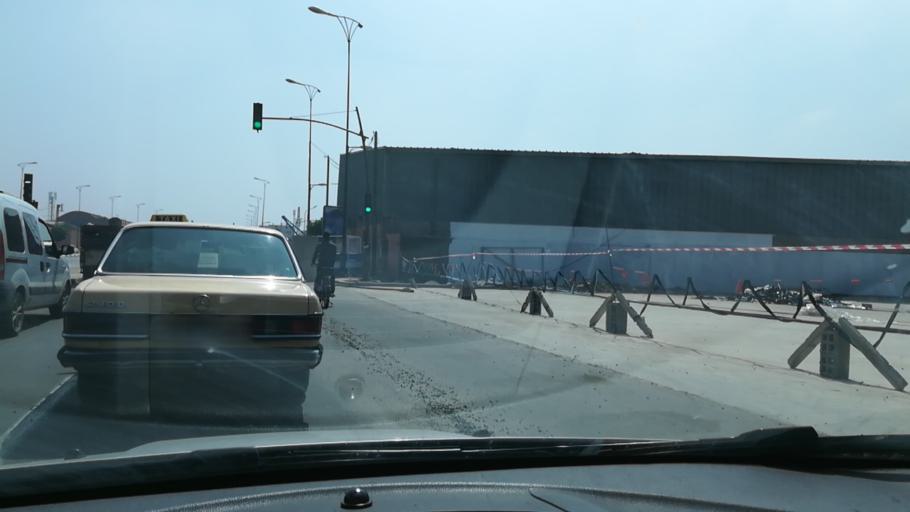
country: MA
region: Marrakech-Tensift-Al Haouz
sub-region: Marrakech
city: Marrakesh
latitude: 31.6269
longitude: -8.0325
